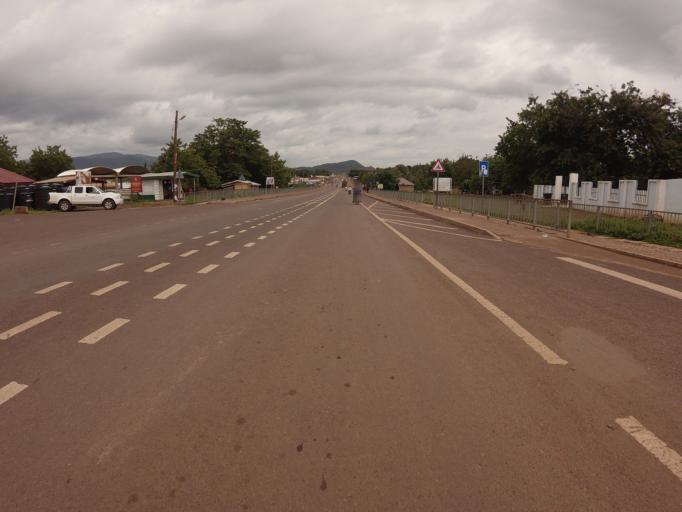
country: TG
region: Centrale
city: Sotouboua
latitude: 8.2568
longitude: 0.5225
